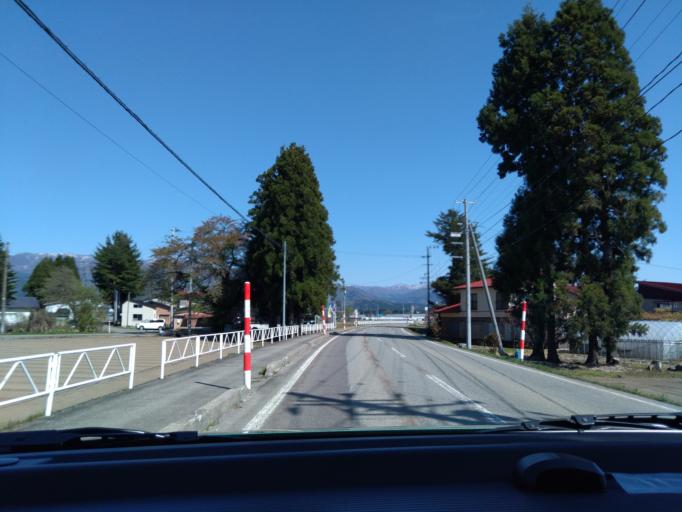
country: JP
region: Akita
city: Kakunodatemachi
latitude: 39.5745
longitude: 140.5735
